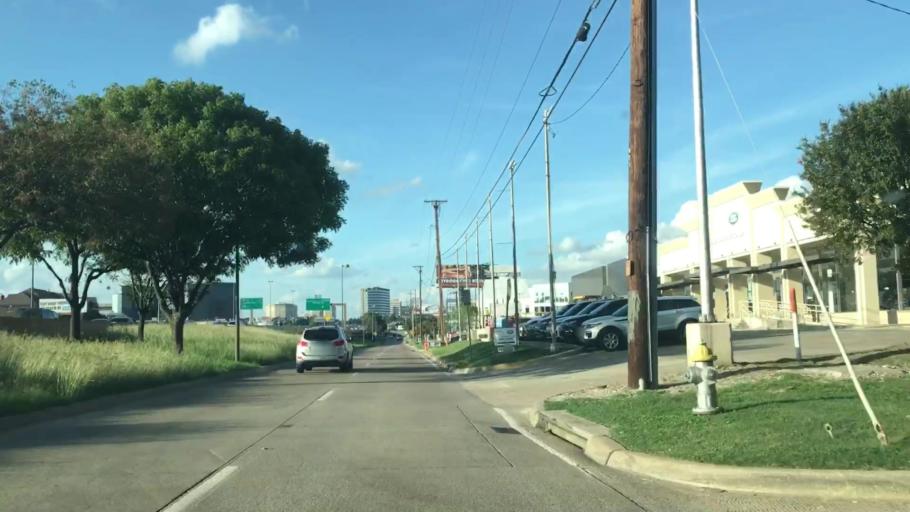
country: US
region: Texas
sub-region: Dallas County
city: University Park
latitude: 32.9017
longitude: -96.7686
